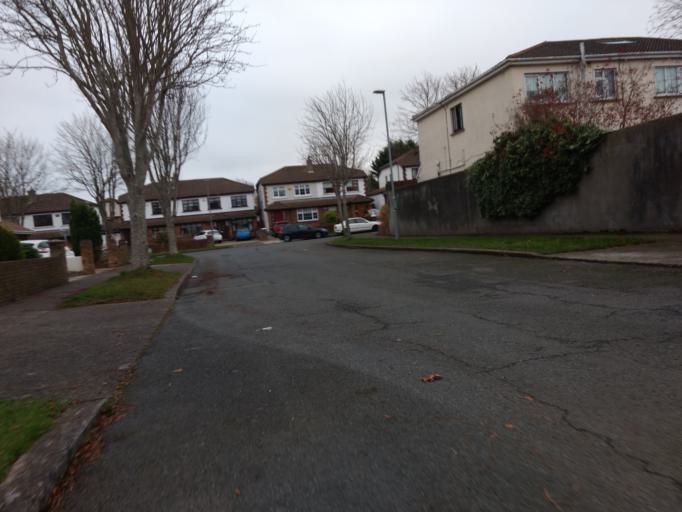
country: IE
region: Leinster
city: Kinsealy-Drinan
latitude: 53.4541
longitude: -6.1803
